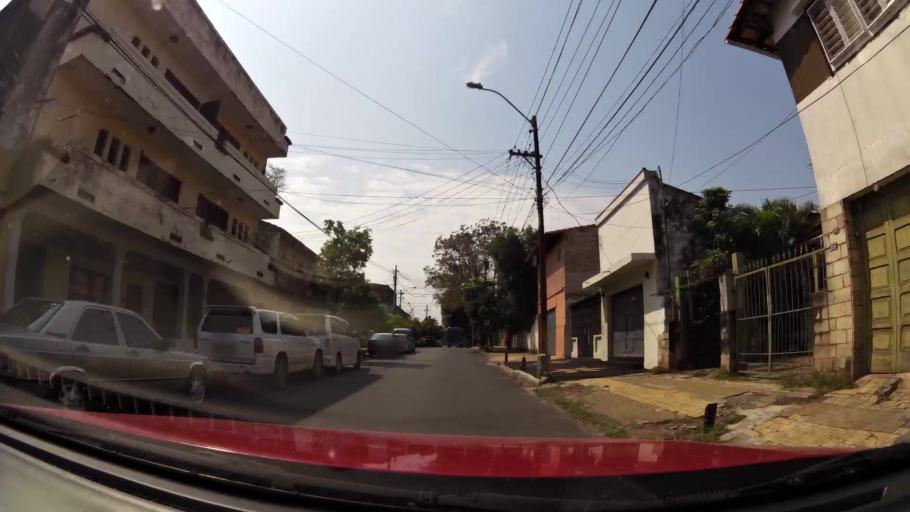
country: PY
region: Asuncion
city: Asuncion
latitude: -25.2958
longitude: -57.6345
